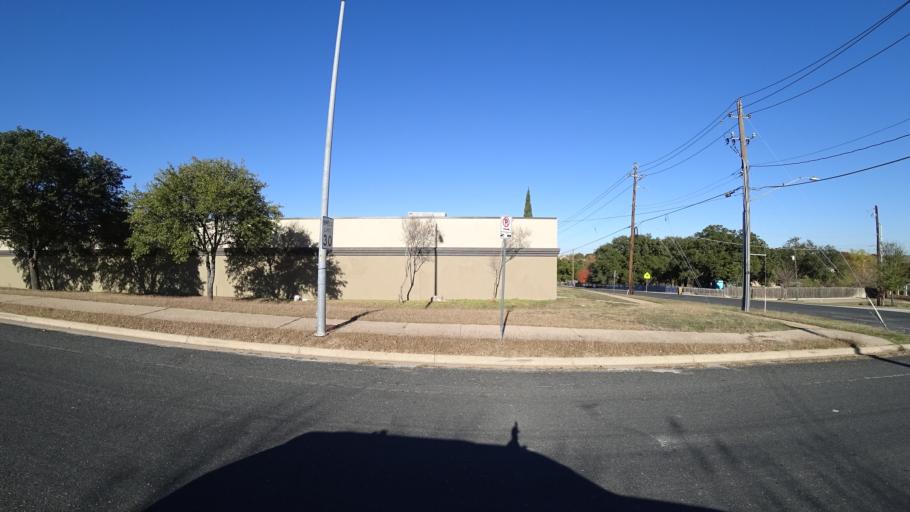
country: US
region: Texas
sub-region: Travis County
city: Wells Branch
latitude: 30.4084
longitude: -97.6932
